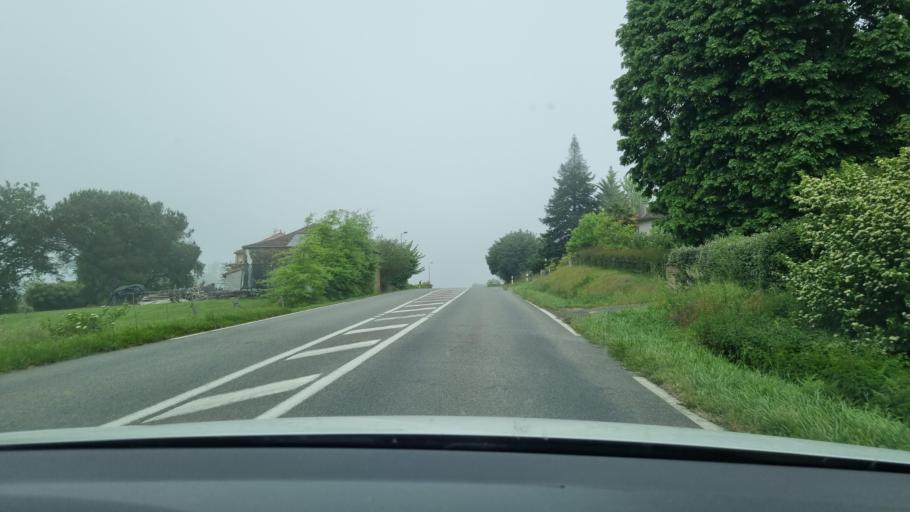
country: FR
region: Aquitaine
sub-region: Departement des Landes
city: Hagetmau
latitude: 43.5888
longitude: -0.6515
